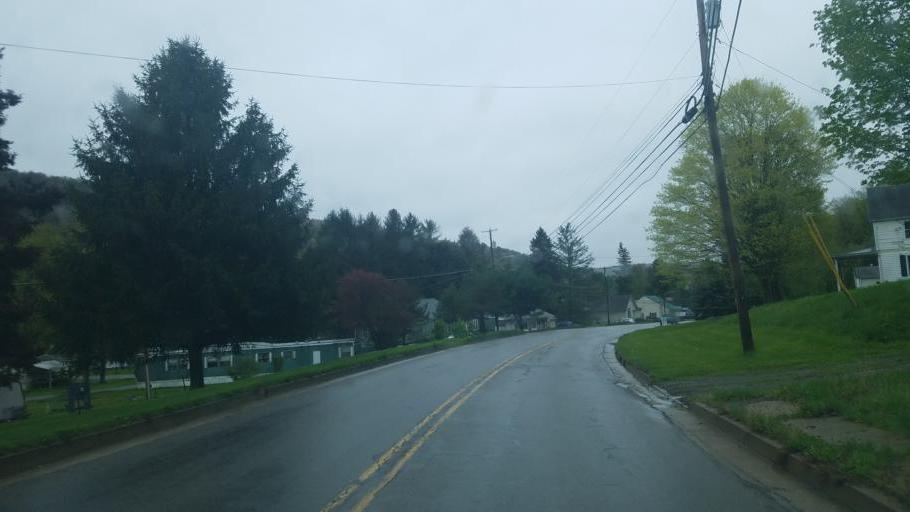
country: US
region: Pennsylvania
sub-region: Potter County
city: Coudersport
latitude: 41.7864
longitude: -78.0170
